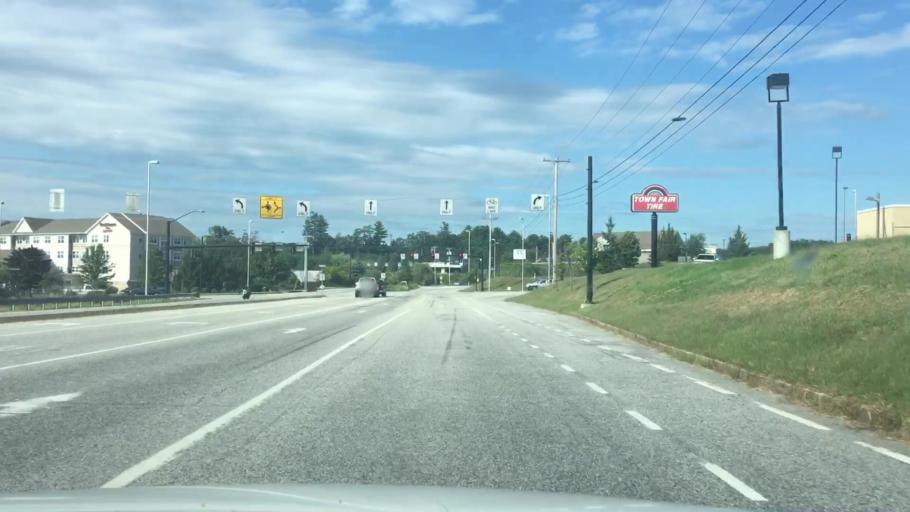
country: US
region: Maine
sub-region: Androscoggin County
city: Auburn
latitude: 44.1207
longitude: -70.2317
